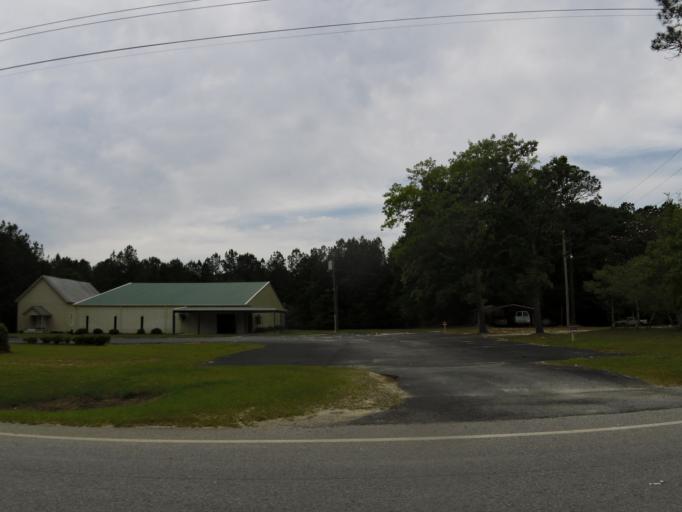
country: US
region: Georgia
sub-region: Emanuel County
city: Twin City
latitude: 32.4370
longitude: -82.2152
